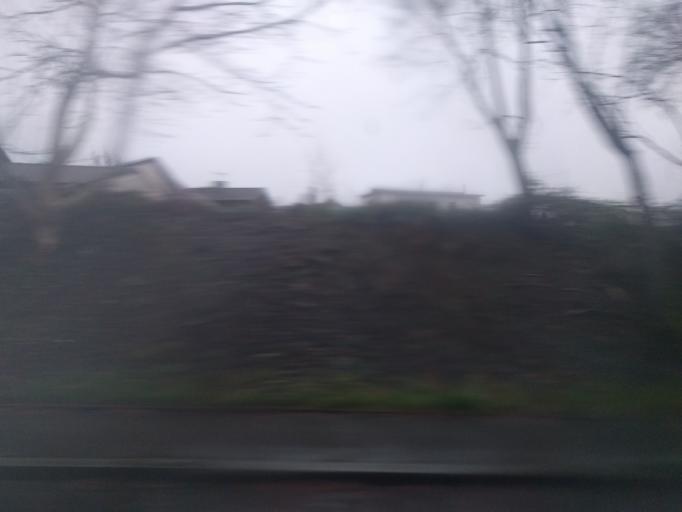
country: DE
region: Bavaria
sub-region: Swabia
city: Nonnenhorn
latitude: 47.5739
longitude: 9.6354
